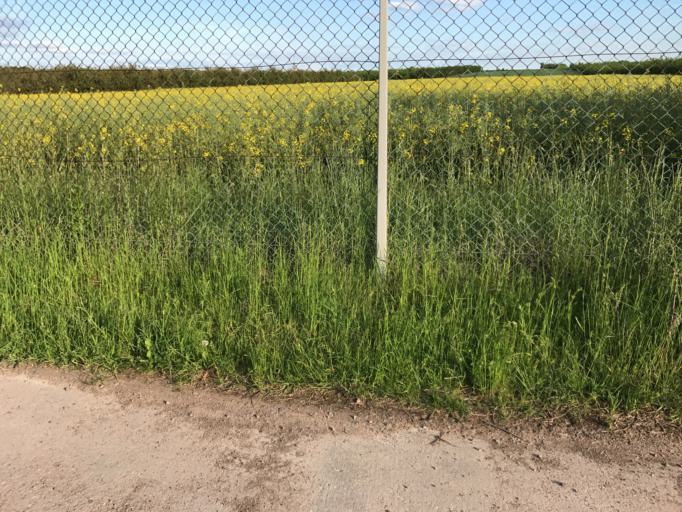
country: DE
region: Rheinland-Pfalz
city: Wackernheim
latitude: 49.9636
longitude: 8.1480
